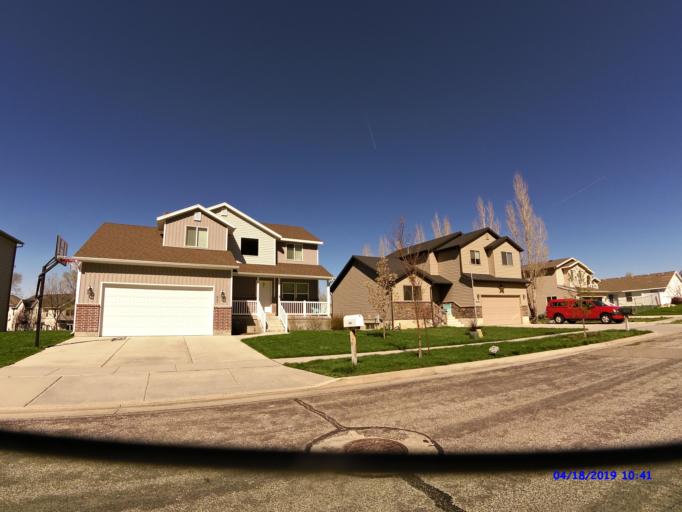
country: US
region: Utah
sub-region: Weber County
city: Harrisville
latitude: 41.2673
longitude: -111.9615
